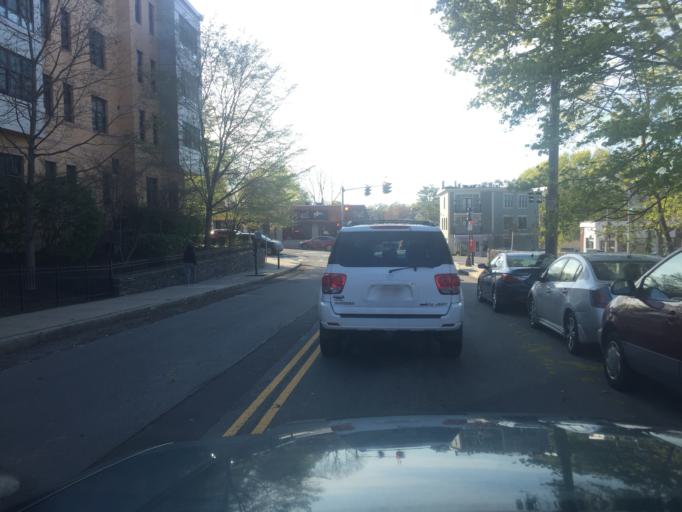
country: US
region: Massachusetts
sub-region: Suffolk County
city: Jamaica Plain
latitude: 42.2780
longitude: -71.1366
